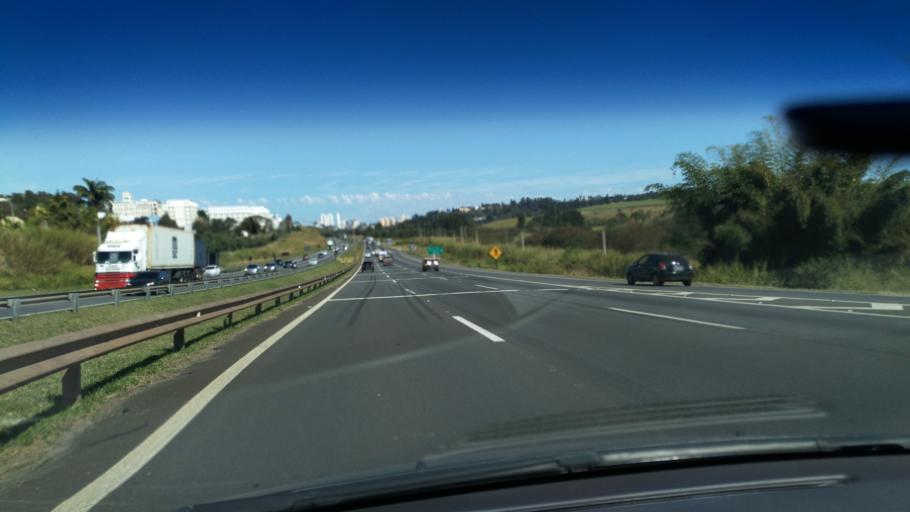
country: BR
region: Sao Paulo
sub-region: Campinas
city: Campinas
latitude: -22.8130
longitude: -47.0352
